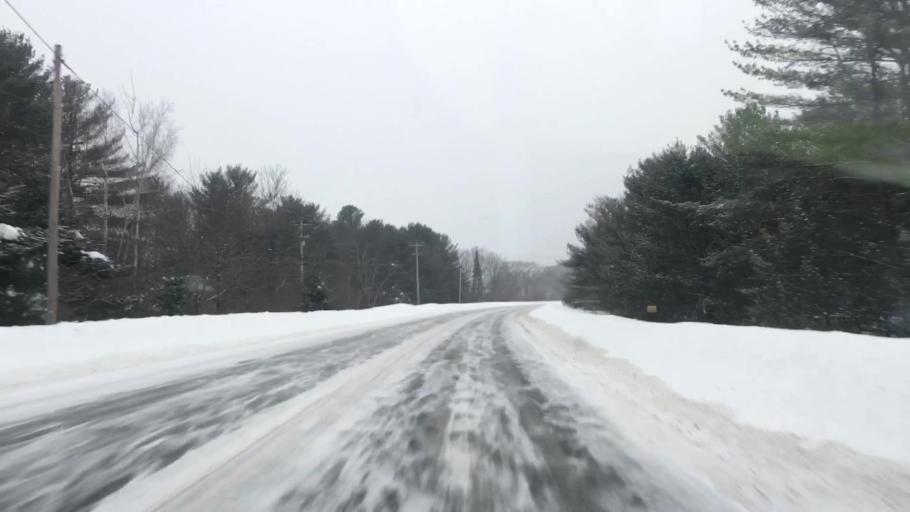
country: US
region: Maine
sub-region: Penobscot County
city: Medway
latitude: 45.5649
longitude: -68.3994
